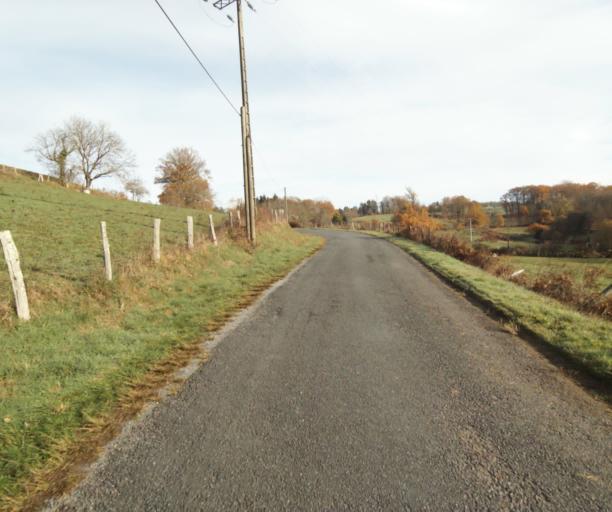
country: FR
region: Limousin
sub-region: Departement de la Correze
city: Chameyrat
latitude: 45.2279
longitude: 1.7269
